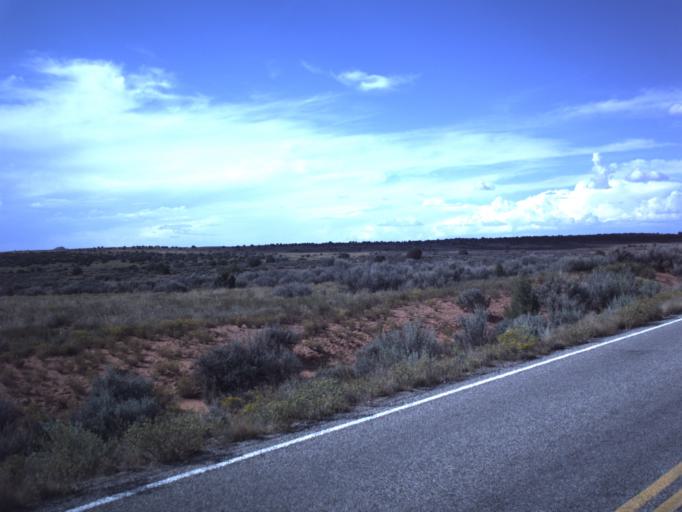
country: US
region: Utah
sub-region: Grand County
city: Moab
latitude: 38.5112
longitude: -109.7293
